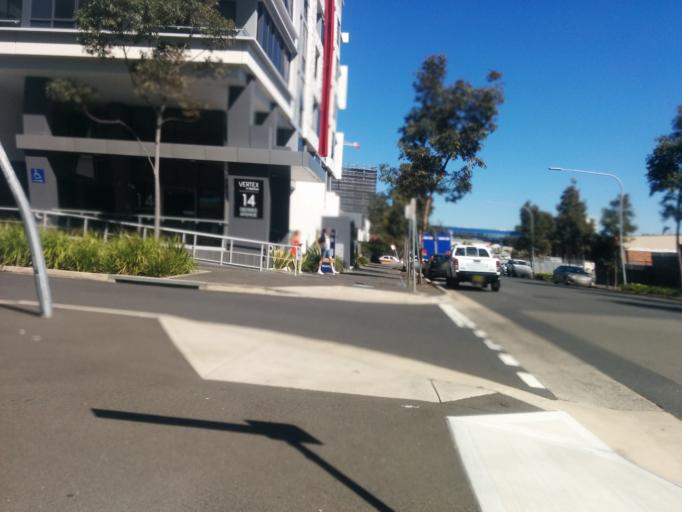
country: AU
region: New South Wales
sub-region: City of Sydney
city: Alexandria
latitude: -33.9090
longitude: 151.2116
